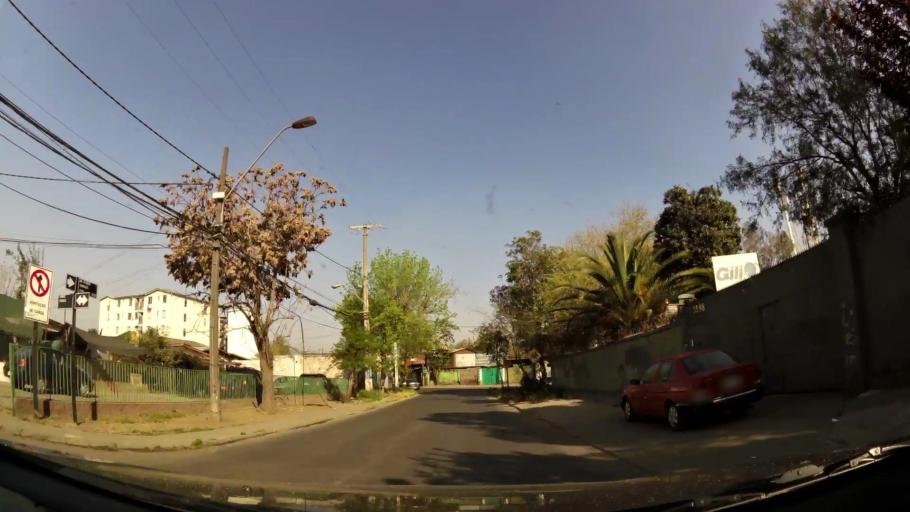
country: CL
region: Santiago Metropolitan
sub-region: Provincia de Santiago
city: Santiago
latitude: -33.3966
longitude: -70.6747
